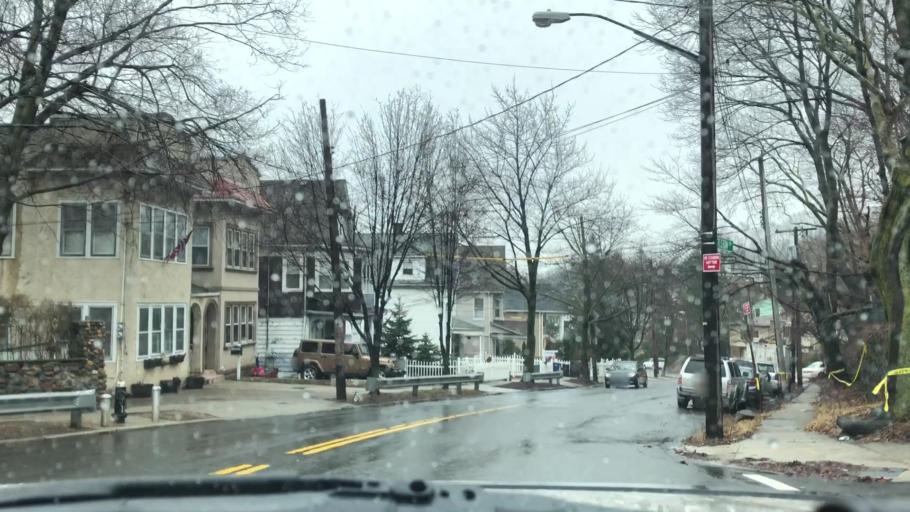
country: US
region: New Jersey
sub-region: Hudson County
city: Bayonne
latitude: 40.6332
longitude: -74.0921
